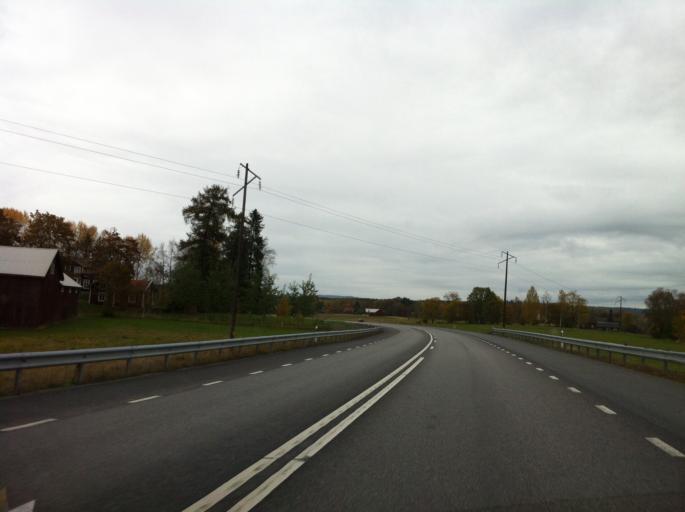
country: SE
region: OErebro
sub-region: Lindesbergs Kommun
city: Stora
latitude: 59.7475
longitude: 15.1428
